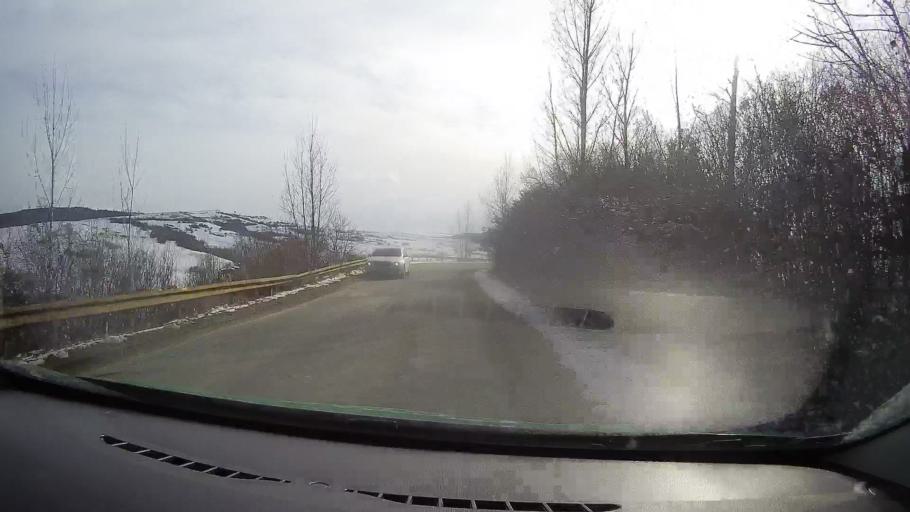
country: RO
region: Sibiu
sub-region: Comuna Bradeni
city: Bradeni
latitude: 46.1042
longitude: 24.8409
